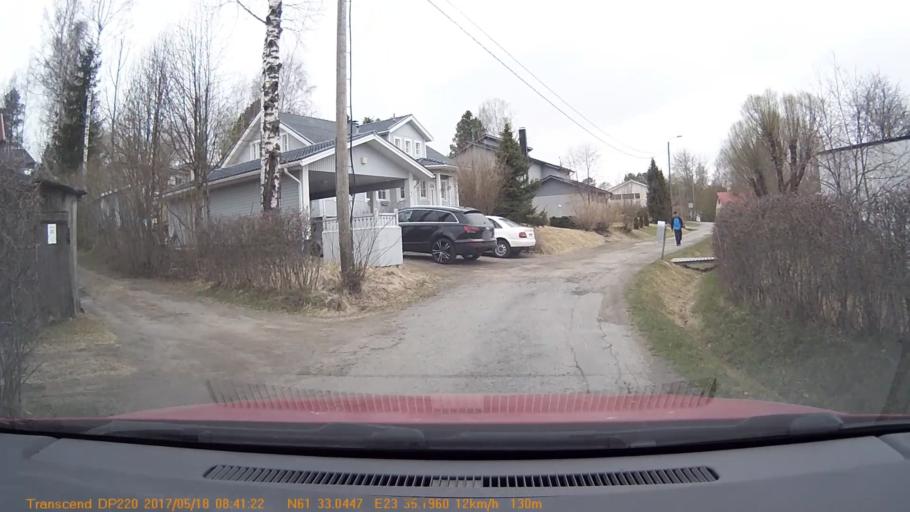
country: FI
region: Pirkanmaa
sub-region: Tampere
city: Yloejaervi
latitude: 61.5508
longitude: 23.5865
